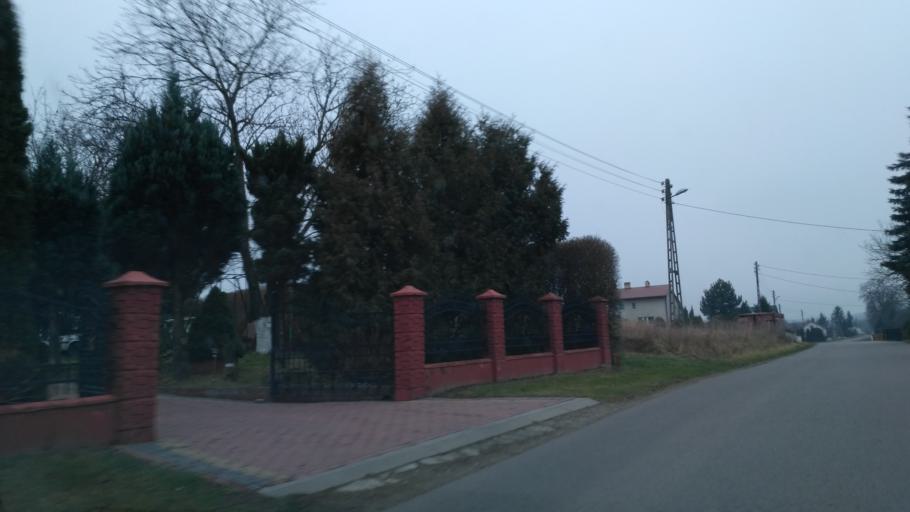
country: PL
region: Subcarpathian Voivodeship
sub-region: Powiat jaroslawski
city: Pawlosiow
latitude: 49.9681
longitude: 22.6440
